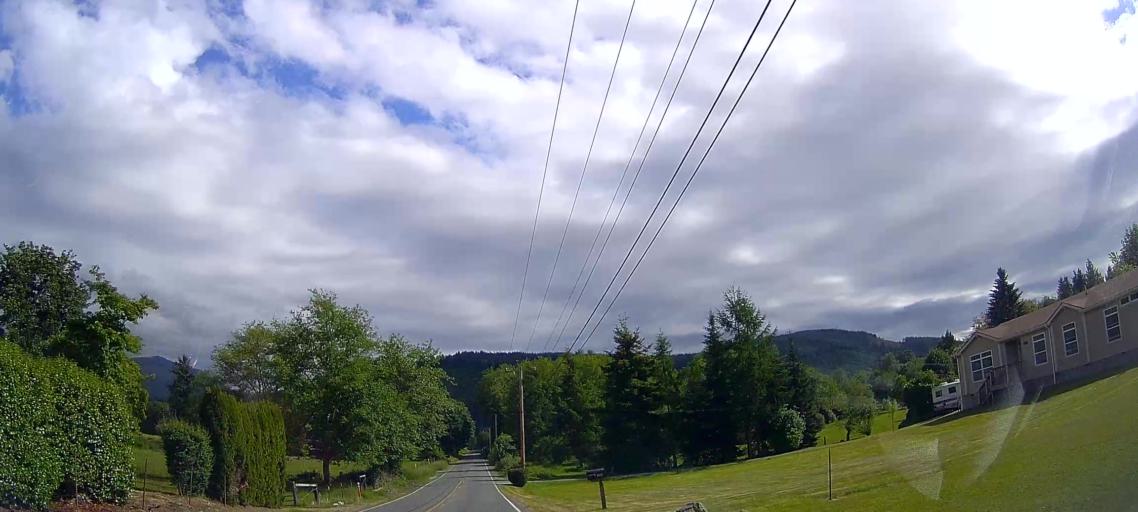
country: US
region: Washington
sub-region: Skagit County
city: Sedro-Woolley
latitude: 48.5000
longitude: -122.2096
